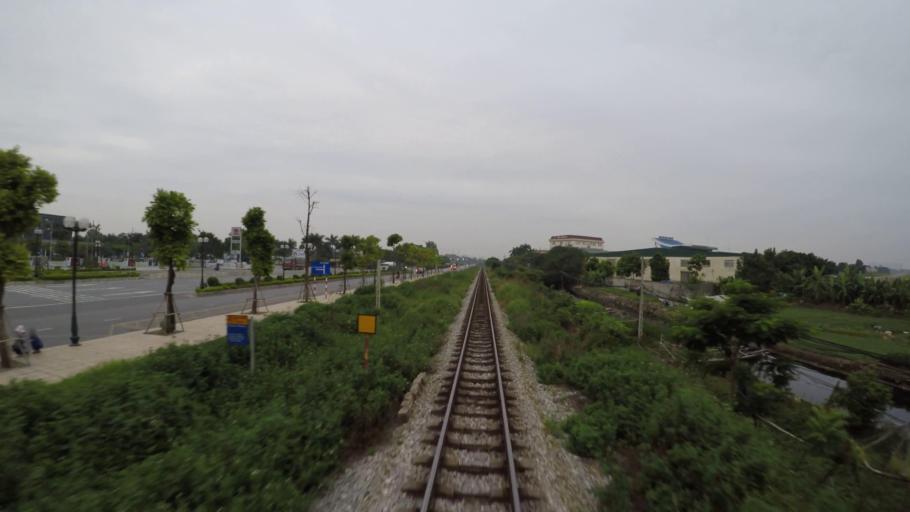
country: VN
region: Ha Noi
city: Trau Quy
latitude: 21.0150
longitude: 105.9466
